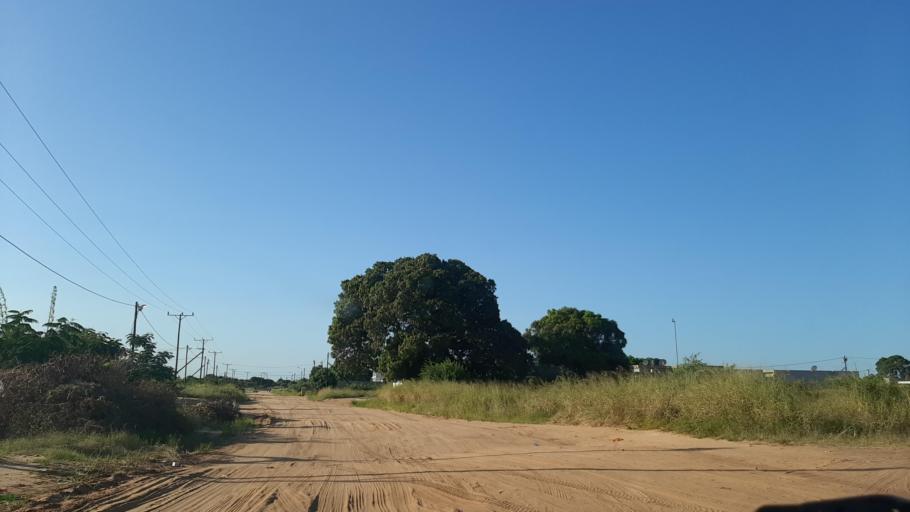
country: MZ
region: Maputo City
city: Maputo
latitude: -25.7687
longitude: 32.5481
